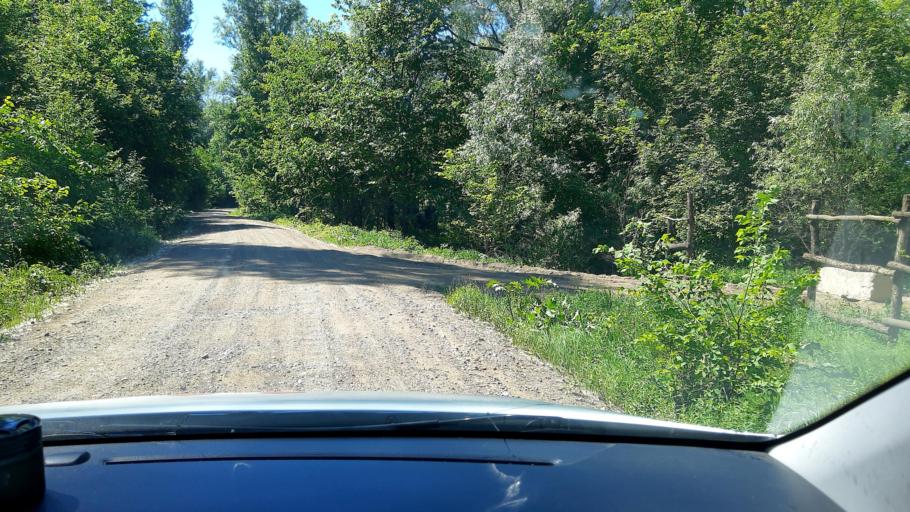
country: RU
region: Bashkortostan
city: Mikhaylovka
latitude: 54.7384
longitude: 55.8579
